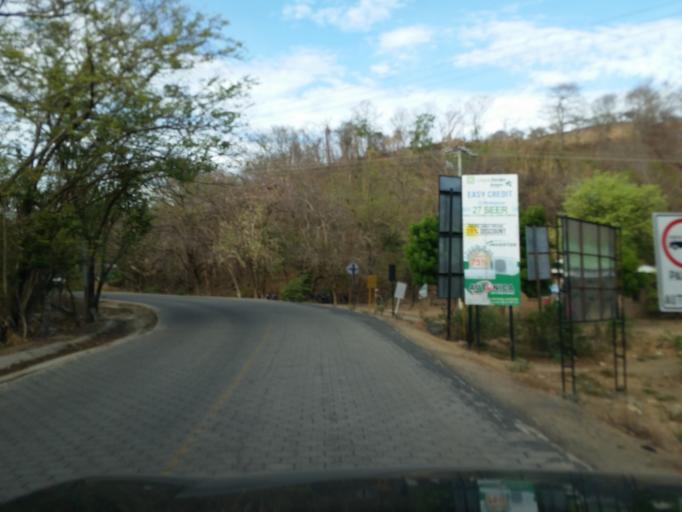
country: NI
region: Rivas
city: Tola
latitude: 11.3929
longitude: -85.9607
